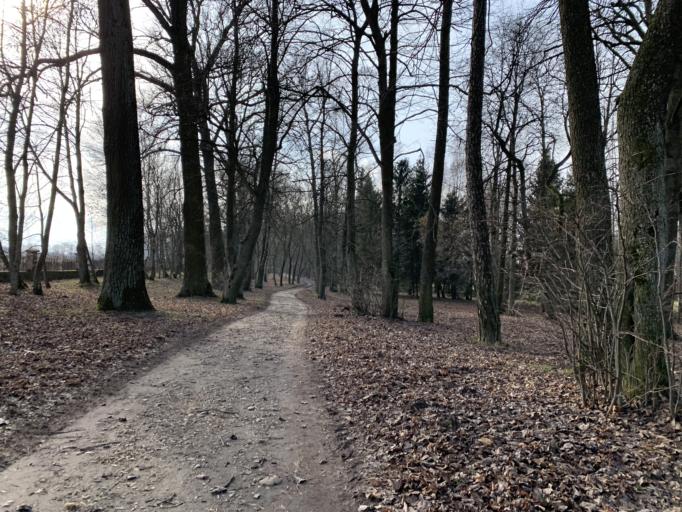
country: BY
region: Minsk
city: Nyasvizh
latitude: 53.2259
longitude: 26.7065
